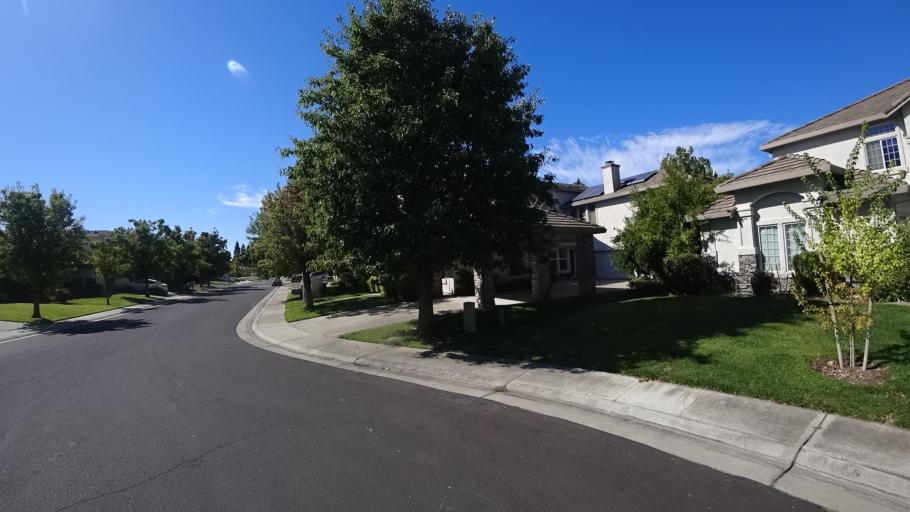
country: US
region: California
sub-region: Sacramento County
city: Laguna
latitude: 38.4222
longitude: -121.4783
